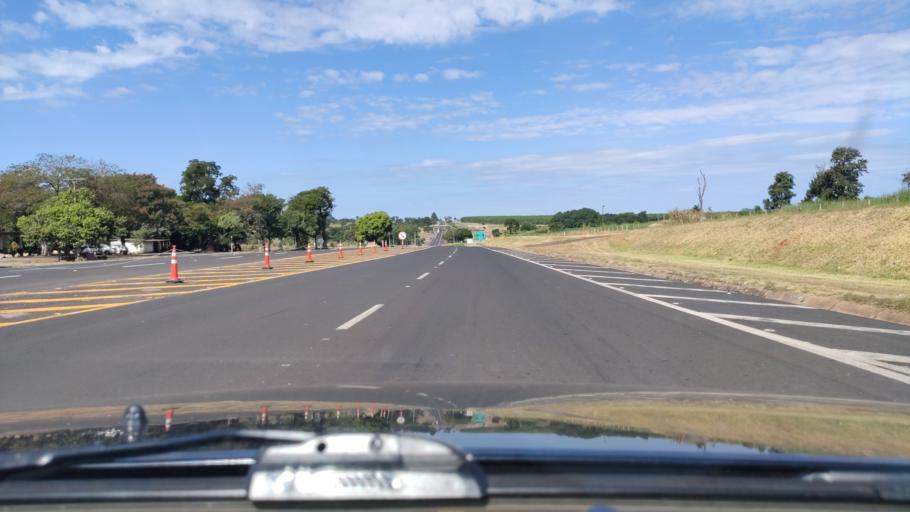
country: BR
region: Sao Paulo
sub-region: Rancharia
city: Rancharia
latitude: -22.4364
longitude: -51.0067
